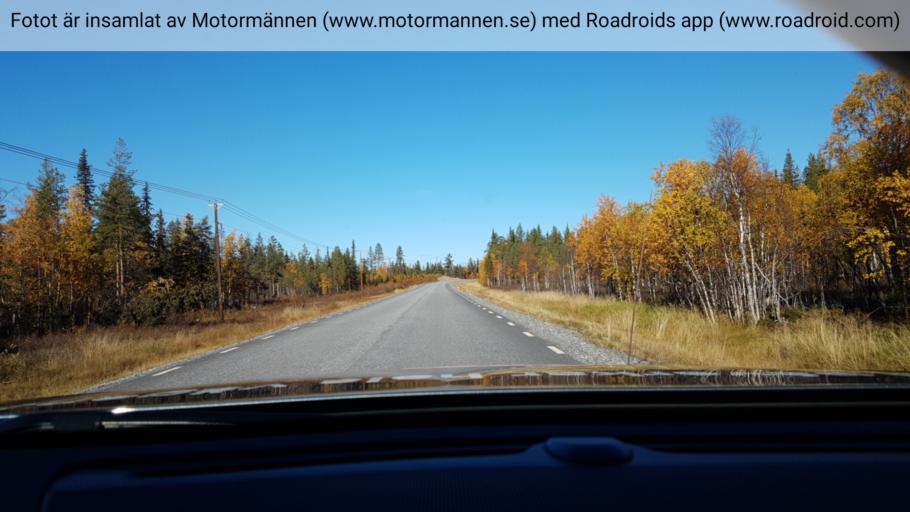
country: SE
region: Norrbotten
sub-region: Gallivare Kommun
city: Gaellivare
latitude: 66.7875
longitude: 21.0400
